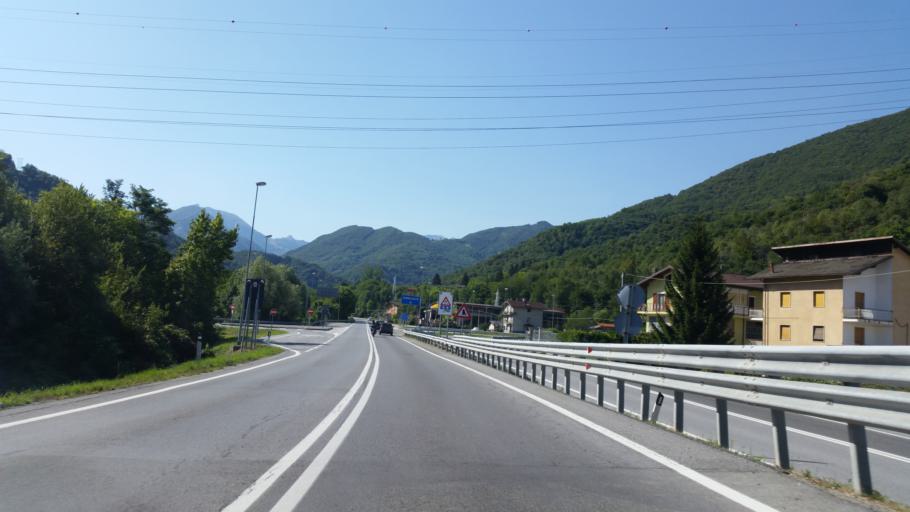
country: IT
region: Piedmont
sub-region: Provincia di Cuneo
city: Robilante
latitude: 44.2812
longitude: 7.5174
